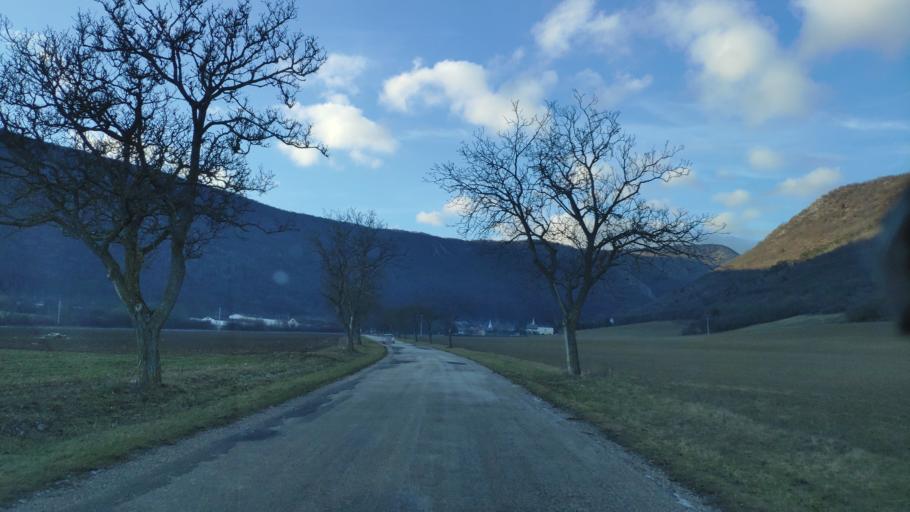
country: SK
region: Kosicky
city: Medzev
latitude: 48.6235
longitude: 20.8658
